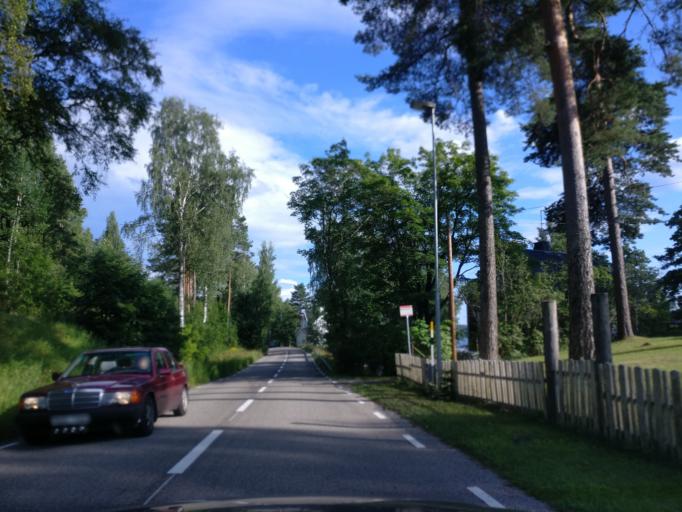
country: SE
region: Dalarna
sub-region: Ludvika Kommun
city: Ludvika
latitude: 60.3085
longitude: 15.2155
